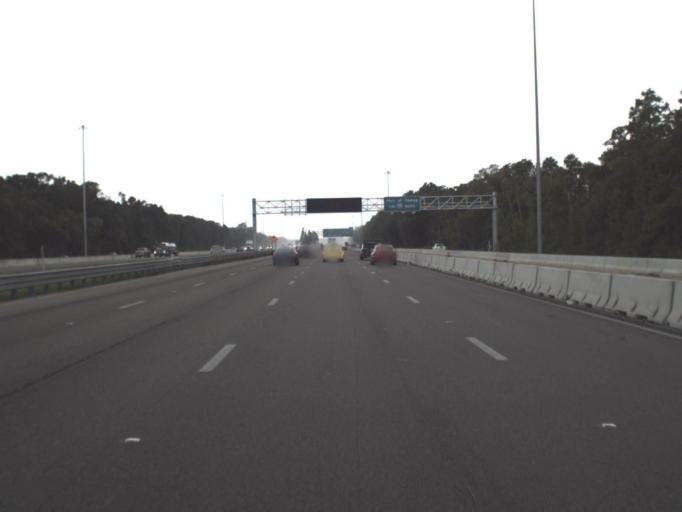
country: US
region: Florida
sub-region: Hillsborough County
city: Pebble Creek
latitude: 28.1886
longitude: -82.3867
